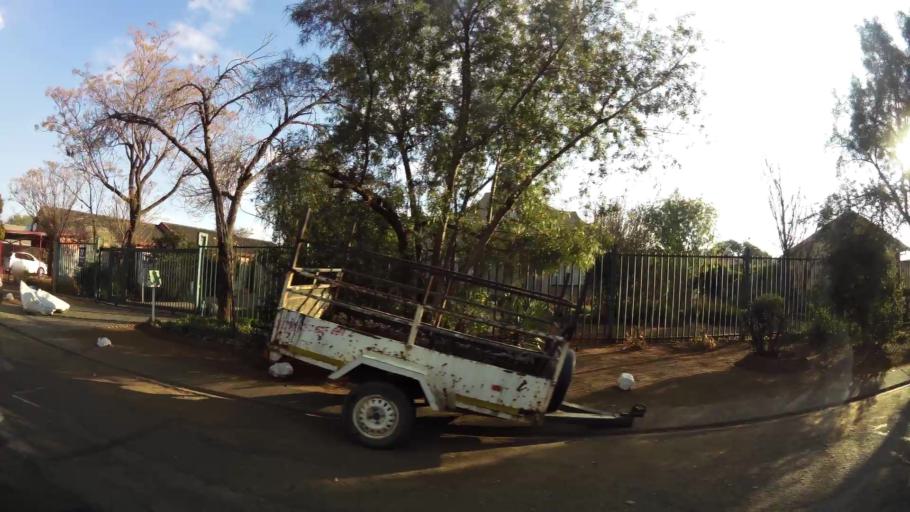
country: ZA
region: Orange Free State
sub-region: Mangaung Metropolitan Municipality
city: Bloemfontein
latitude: -29.1518
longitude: 26.1753
